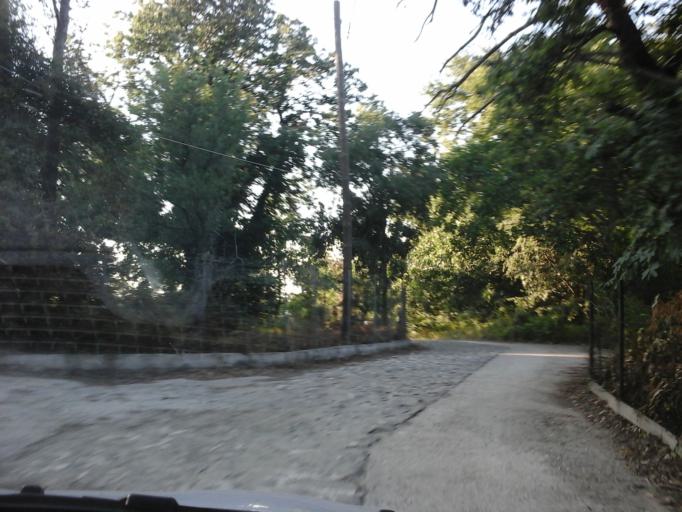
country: GR
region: East Macedonia and Thrace
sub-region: Nomos Evrou
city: Samothraki
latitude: 40.4932
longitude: 25.6117
